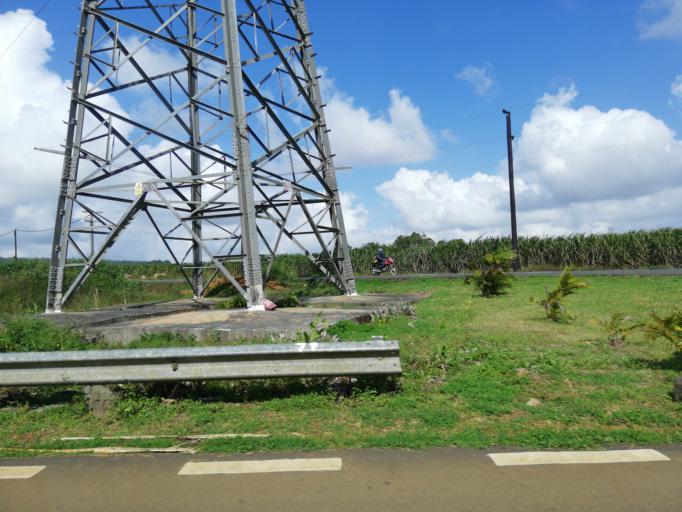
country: MU
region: Moka
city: Verdun
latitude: -20.2122
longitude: 57.5551
